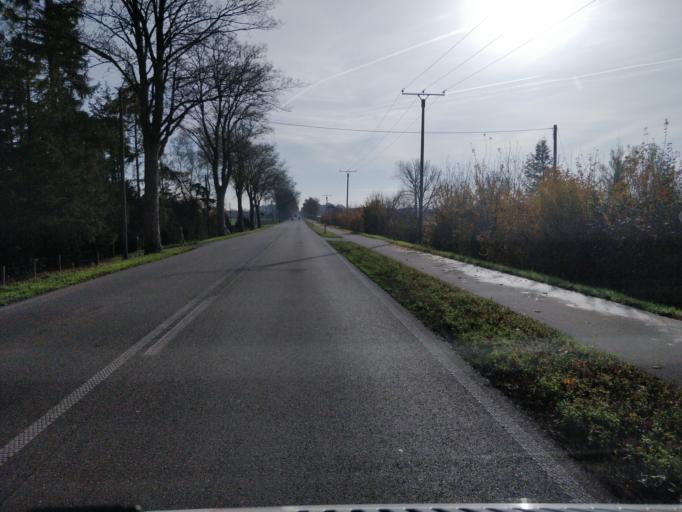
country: DE
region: North Rhine-Westphalia
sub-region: Regierungsbezirk Dusseldorf
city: Mehrhoog
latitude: 51.7537
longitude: 6.4855
